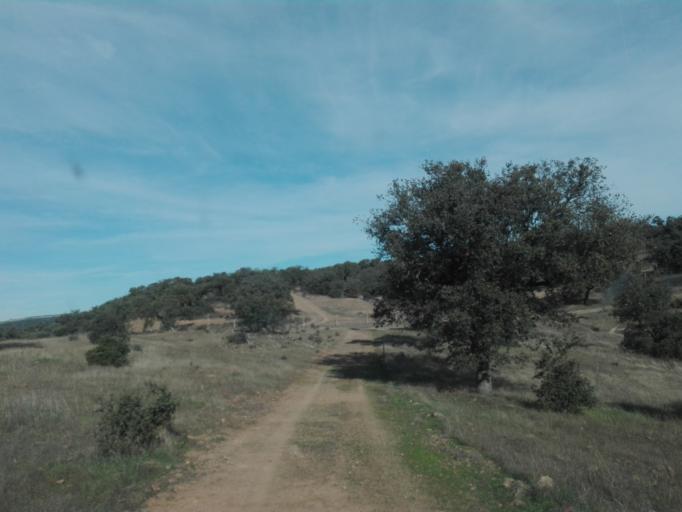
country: ES
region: Extremadura
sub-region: Provincia de Badajoz
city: Valverde de Llerena
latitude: 38.2143
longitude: -5.7470
